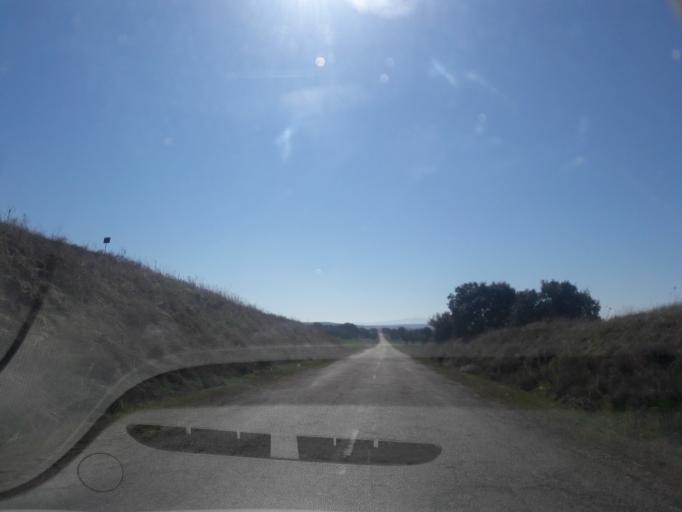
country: ES
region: Castille and Leon
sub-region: Provincia de Salamanca
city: Mancera de Abajo
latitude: 40.8208
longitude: -5.1742
